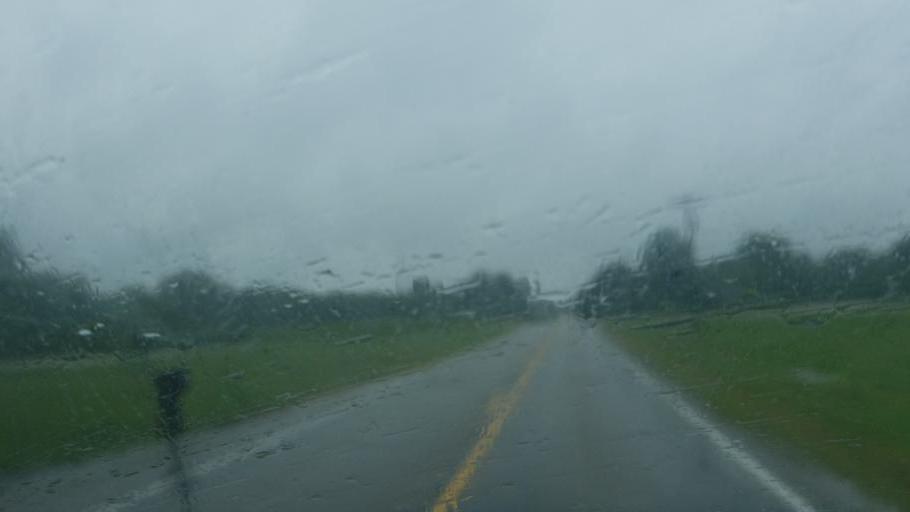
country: US
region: Indiana
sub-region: Huntington County
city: Warren
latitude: 40.6726
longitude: -85.4155
